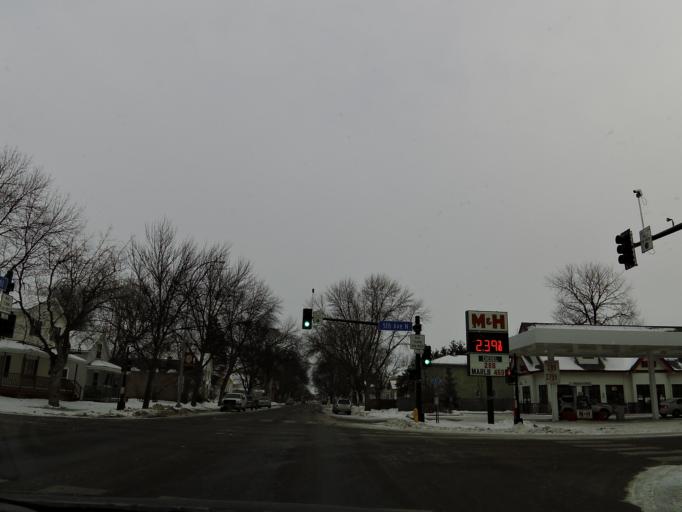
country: US
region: North Dakota
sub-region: Grand Forks County
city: Grand Forks
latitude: 47.9271
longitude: -97.0387
